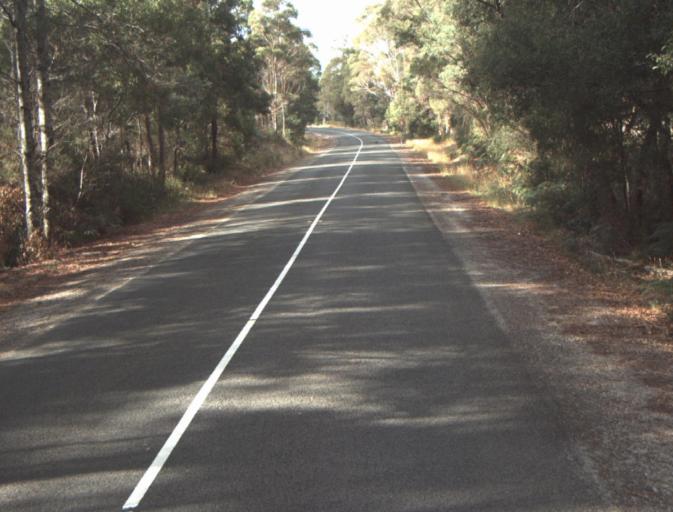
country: AU
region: Tasmania
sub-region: Dorset
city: Bridport
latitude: -41.1189
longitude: 147.2045
